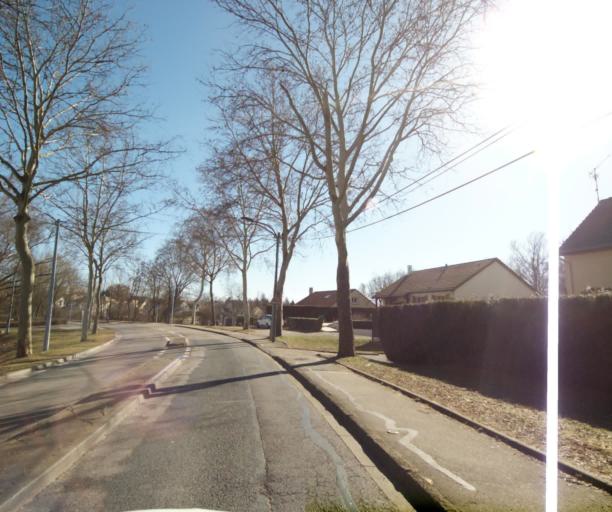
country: FR
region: Lorraine
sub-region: Departement de Meurthe-et-Moselle
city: Heillecourt
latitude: 48.6531
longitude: 6.2032
